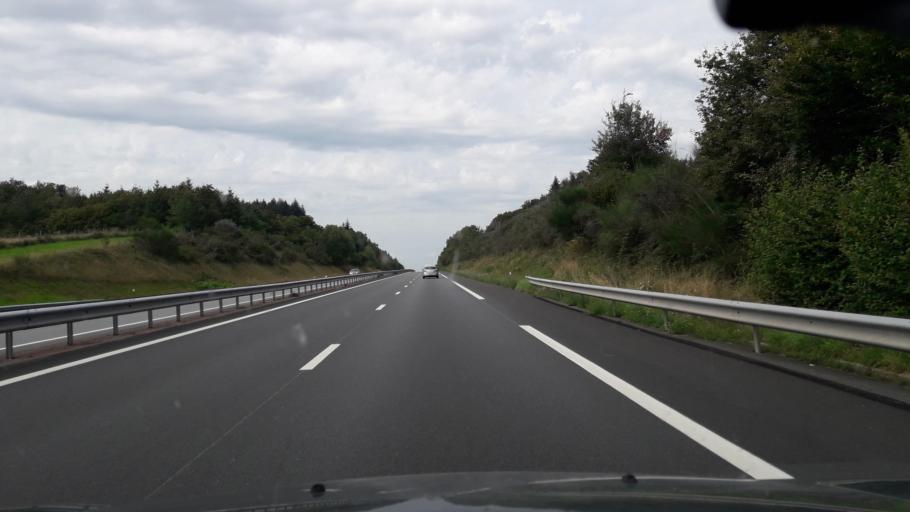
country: FR
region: Limousin
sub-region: Departement de la Creuse
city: Ajain
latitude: 46.2064
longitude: 2.0346
